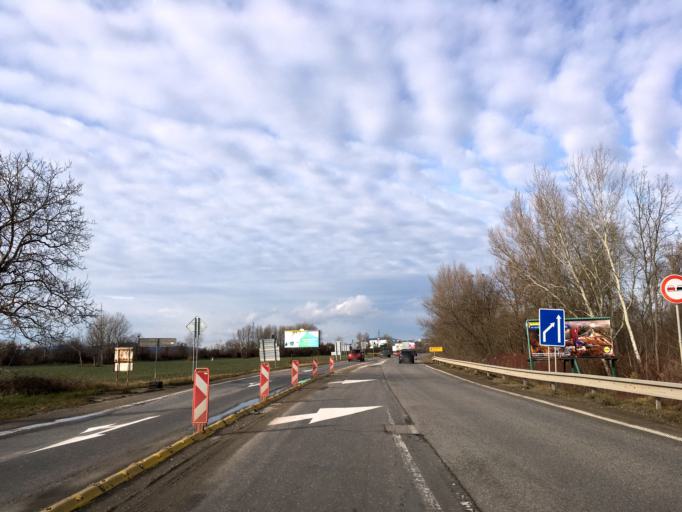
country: AT
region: Burgenland
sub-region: Politischer Bezirk Neusiedl am See
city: Kittsee
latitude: 48.0795
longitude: 17.1280
